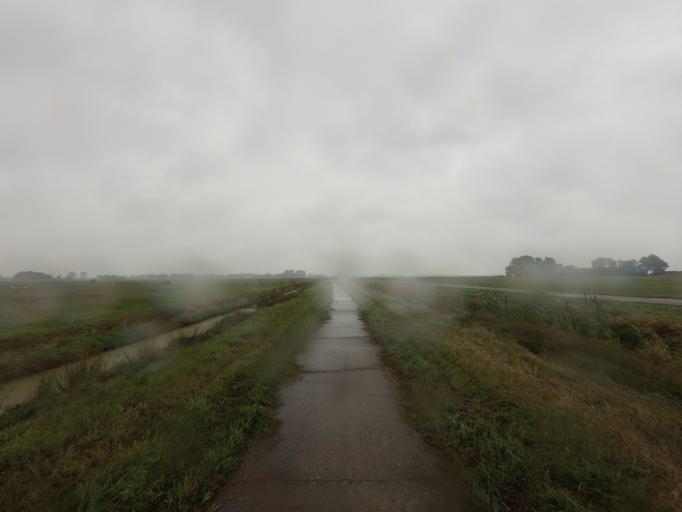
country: NL
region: Friesland
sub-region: Gemeente Boarnsterhim
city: Aldeboarn
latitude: 53.0344
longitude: 5.8854
